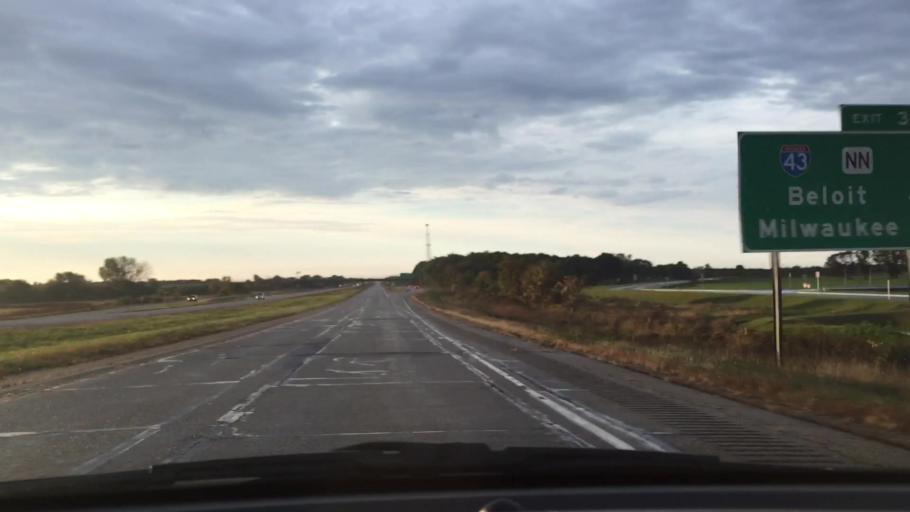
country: US
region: Wisconsin
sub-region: Walworth County
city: Elkhorn
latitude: 42.6813
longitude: -88.5272
